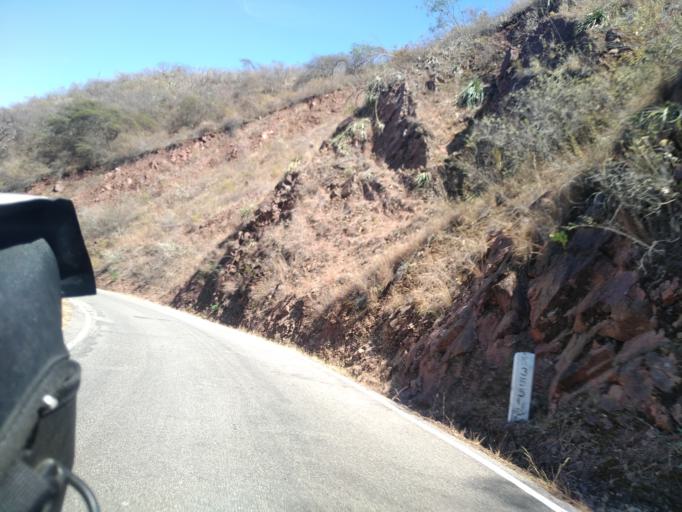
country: PE
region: Amazonas
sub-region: Provincia de Chachapoyas
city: Balsas
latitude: -6.8475
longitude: -77.9664
